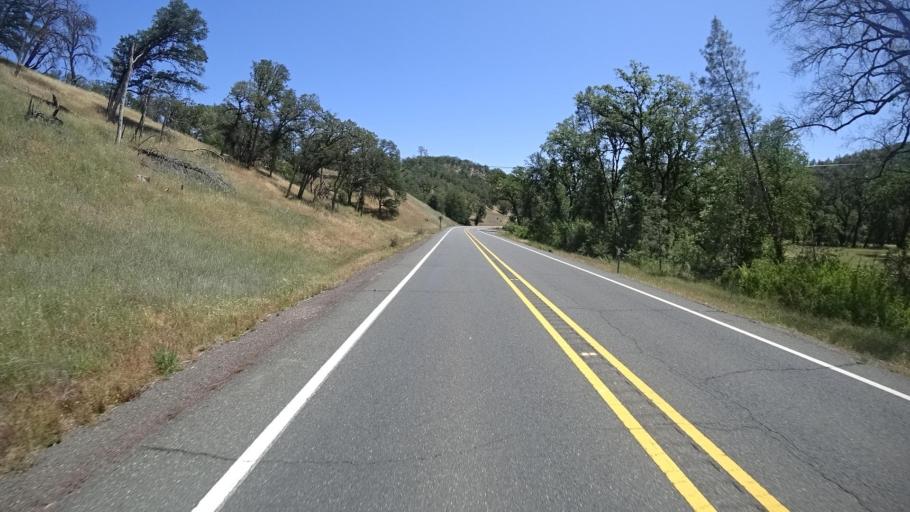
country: US
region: California
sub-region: Lake County
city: Lower Lake
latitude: 38.8567
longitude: -122.6246
